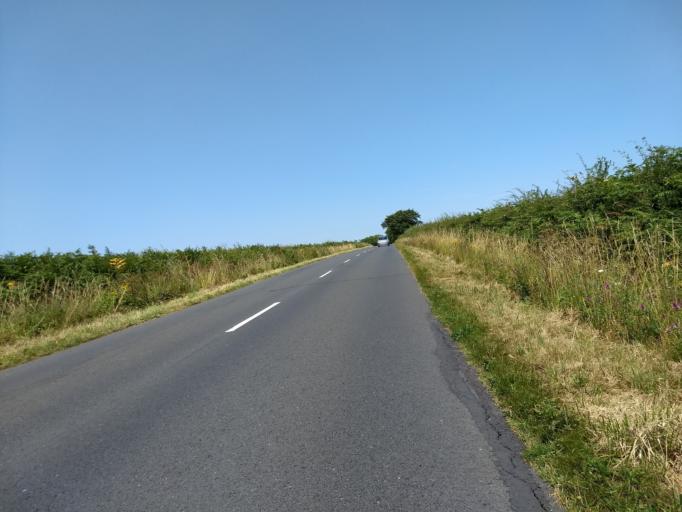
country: GB
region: England
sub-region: Isle of Wight
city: Northwood
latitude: 50.7190
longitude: -1.3526
